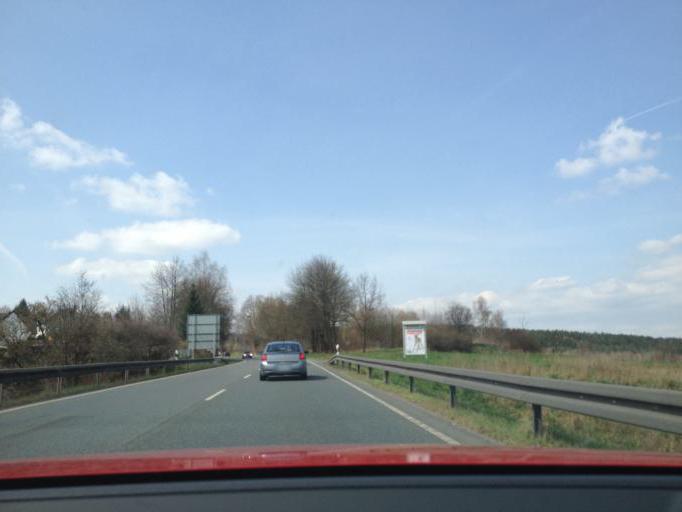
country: DE
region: Bavaria
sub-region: Upper Franconia
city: Marktredwitz
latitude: 50.0151
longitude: 12.0920
